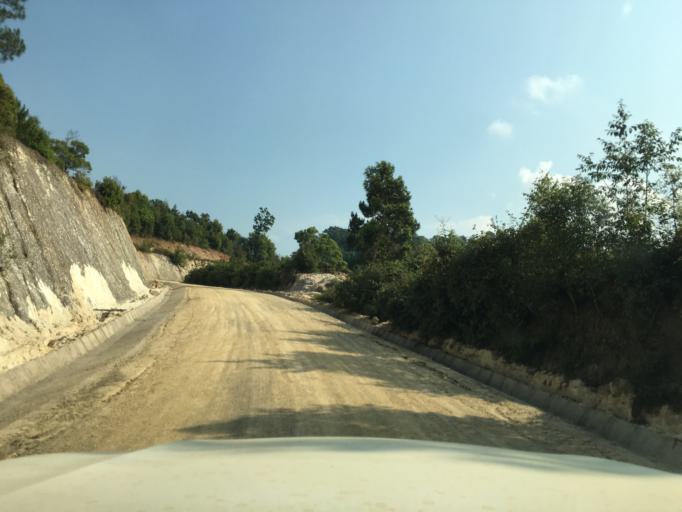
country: LA
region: Houaphan
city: Huameung
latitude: 20.1883
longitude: 103.8343
